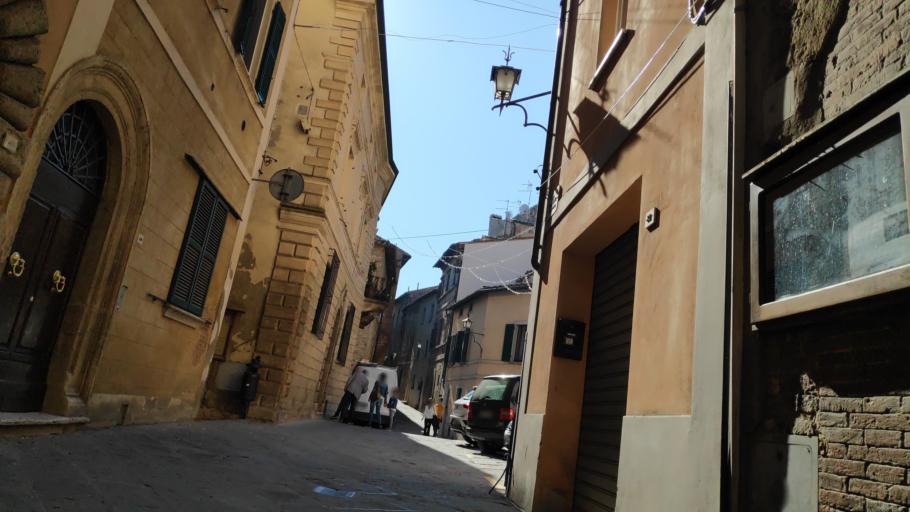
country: IT
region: Tuscany
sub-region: Provincia di Siena
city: Montepulciano
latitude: 43.0915
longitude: 11.7815
